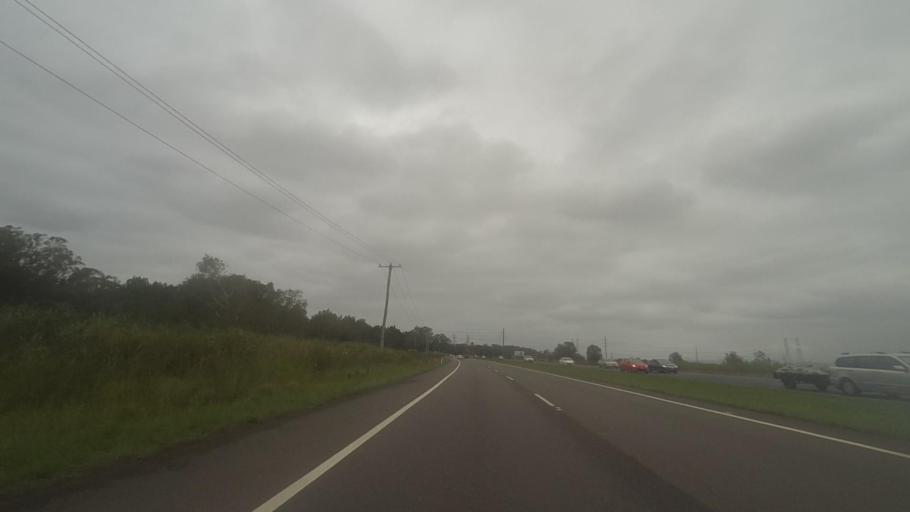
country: AU
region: New South Wales
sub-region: Newcastle
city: Beresfield
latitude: -32.8045
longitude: 151.7132
